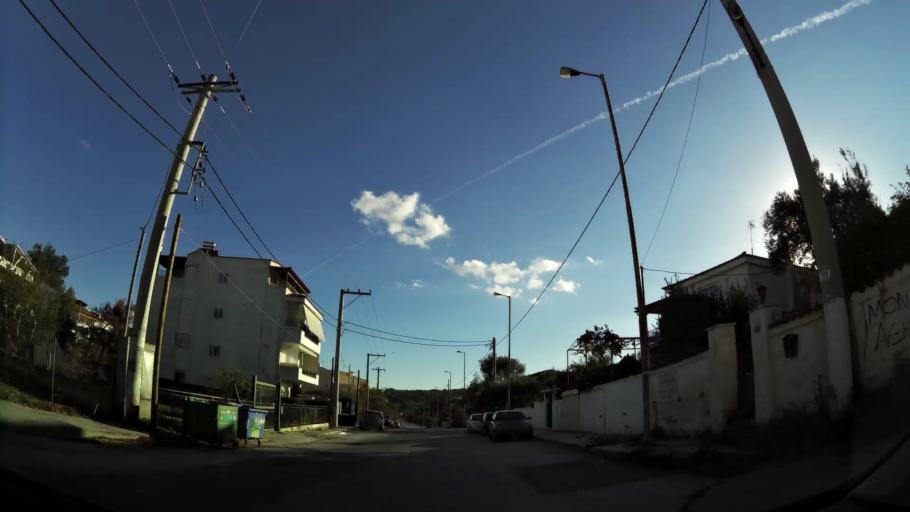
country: GR
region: Attica
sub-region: Nomarchia Anatolikis Attikis
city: Rafina
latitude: 38.0236
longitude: 23.9966
